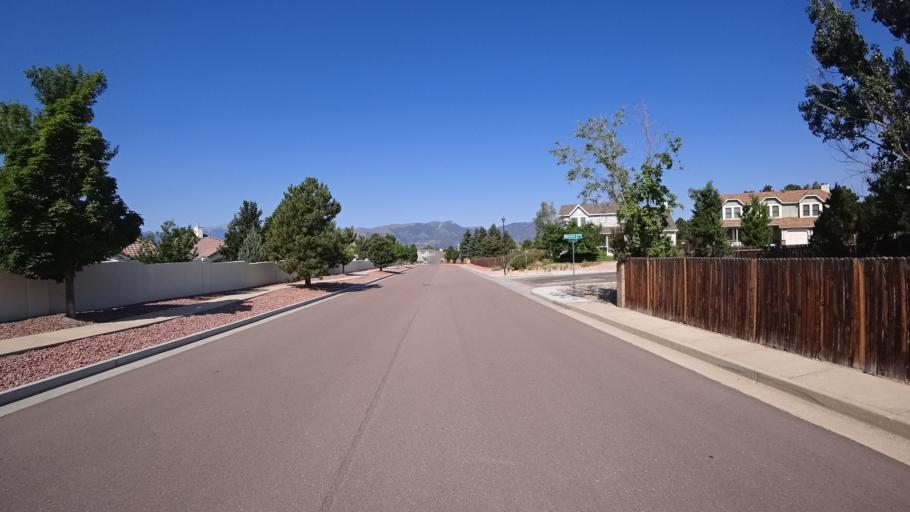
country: US
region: Colorado
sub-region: El Paso County
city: Black Forest
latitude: 38.9555
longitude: -104.7764
